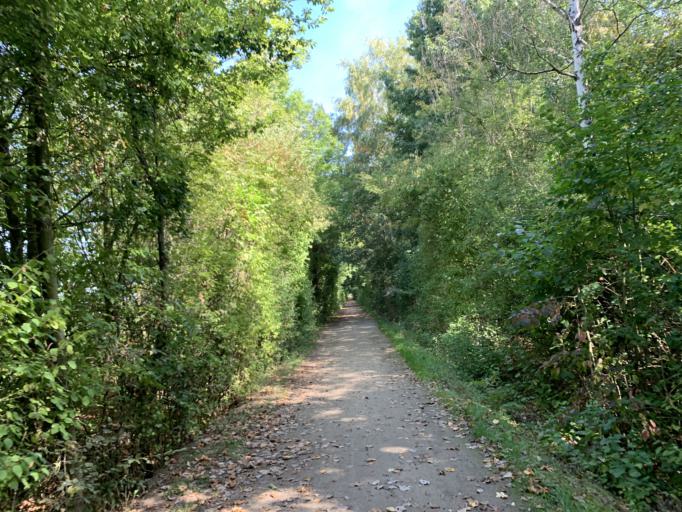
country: DE
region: North Rhine-Westphalia
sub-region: Regierungsbezirk Koln
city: Dueren
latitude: 50.8060
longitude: 6.4378
